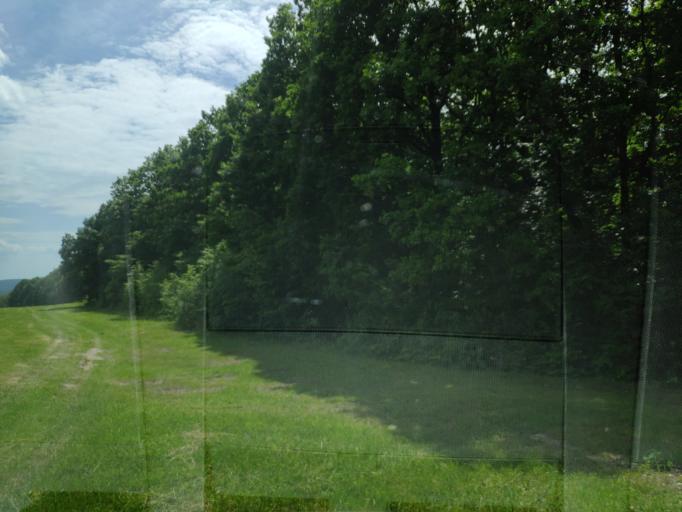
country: SK
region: Kosicky
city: Medzev
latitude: 48.7208
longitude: 20.9540
